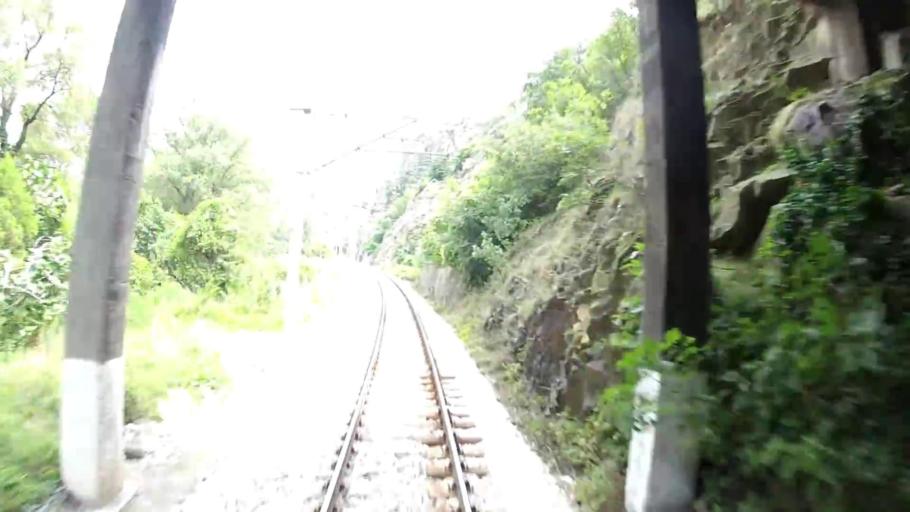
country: BG
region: Blagoevgrad
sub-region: Obshtina Kresna
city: Stara Kresna
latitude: 41.8224
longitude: 23.1600
